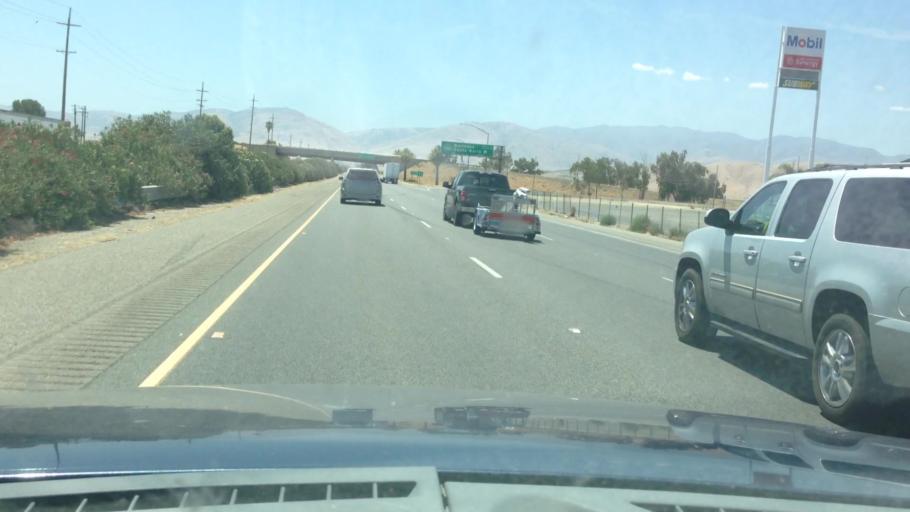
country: US
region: California
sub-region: Kern County
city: Weedpatch
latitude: 35.0613
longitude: -118.9689
